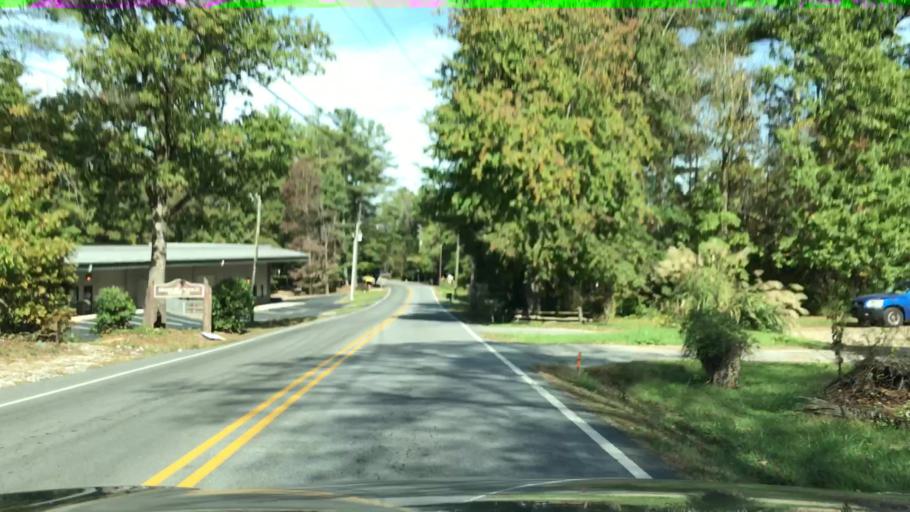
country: US
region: North Carolina
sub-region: Buncombe County
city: Royal Pines
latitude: 35.4531
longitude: -82.5262
